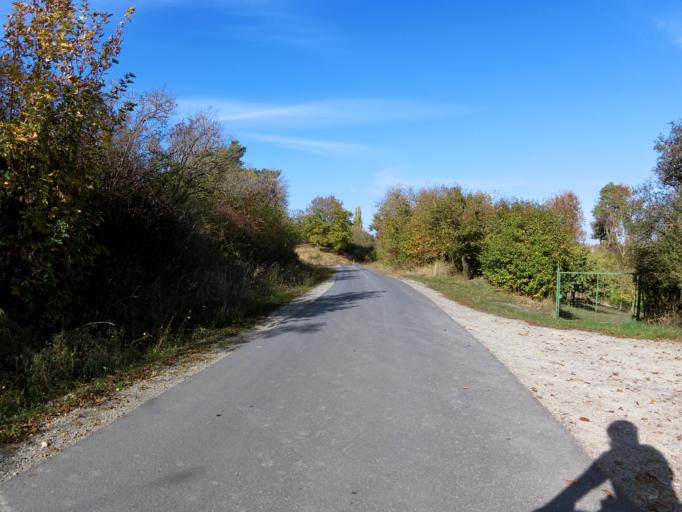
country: DE
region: Bavaria
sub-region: Regierungsbezirk Unterfranken
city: Eibelstadt
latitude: 49.7087
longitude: 9.9936
